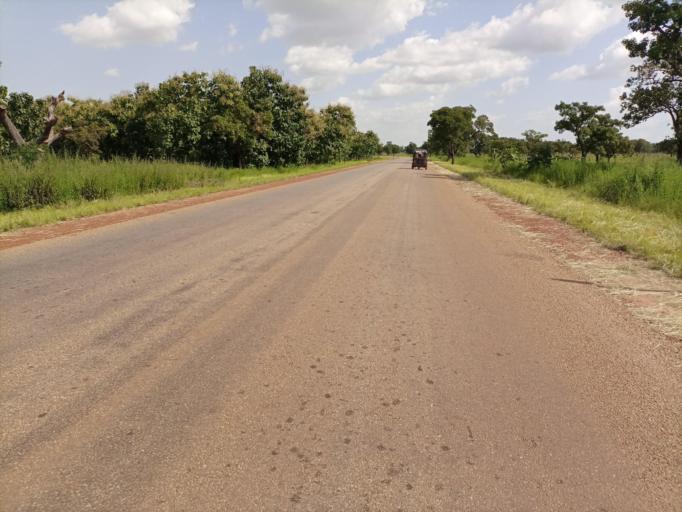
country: GH
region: Northern
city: Savelugu
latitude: 9.5676
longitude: -0.9884
